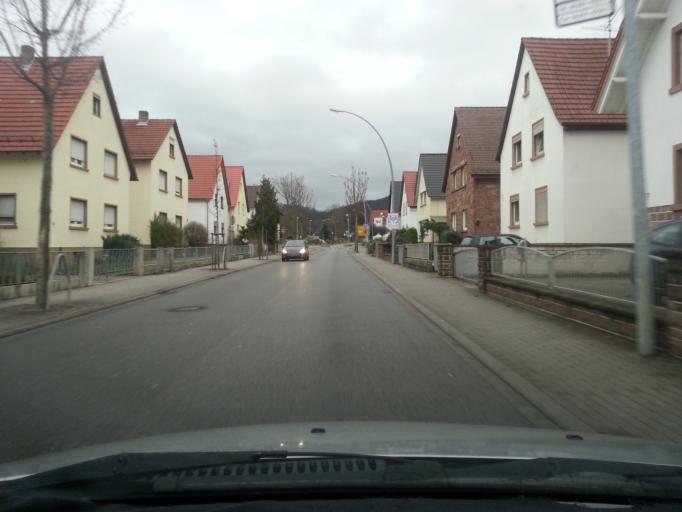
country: DE
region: Baden-Wuerttemberg
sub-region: Karlsruhe Region
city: Hemsbach
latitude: 49.5919
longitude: 8.6436
